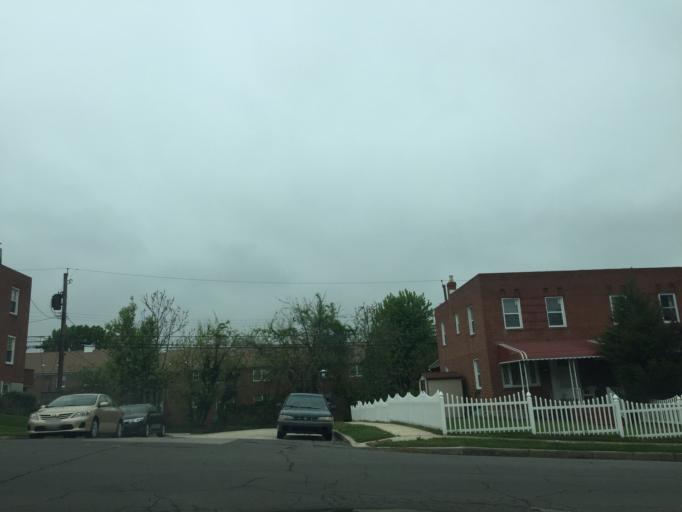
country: US
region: Maryland
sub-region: City of Baltimore
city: Baltimore
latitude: 39.3437
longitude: -76.6444
